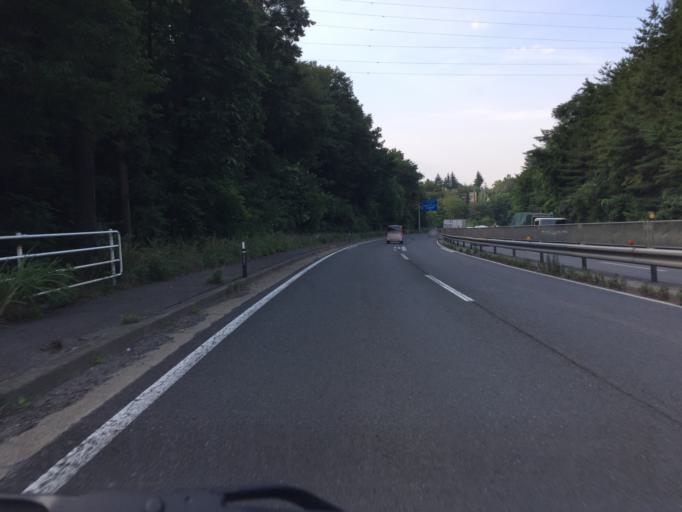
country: JP
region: Fukushima
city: Fukushima-shi
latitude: 37.7077
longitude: 140.4633
